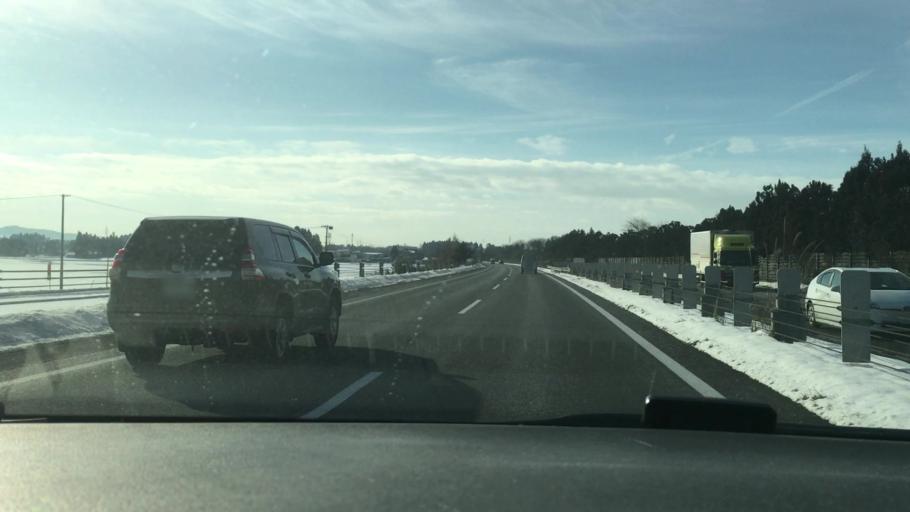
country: JP
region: Iwate
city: Hanamaki
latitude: 39.3584
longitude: 141.0896
